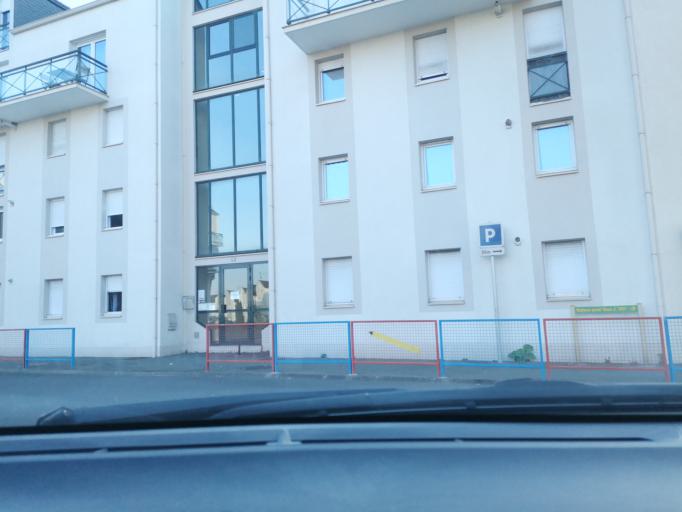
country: FR
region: Centre
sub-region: Departement du Loiret
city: Fleury-les-Aubrais
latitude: 47.9397
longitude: 1.9307
